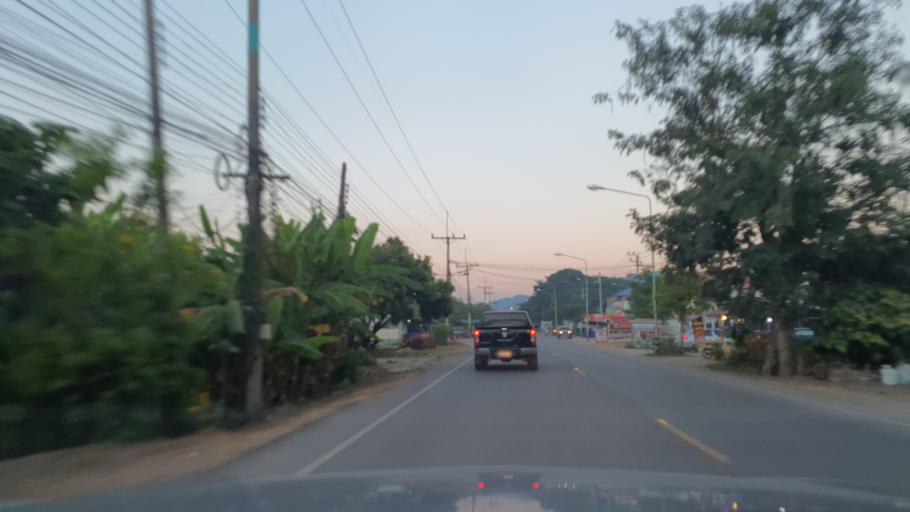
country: TH
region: Phayao
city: Dok Kham Tai
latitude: 19.0889
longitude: 100.0643
